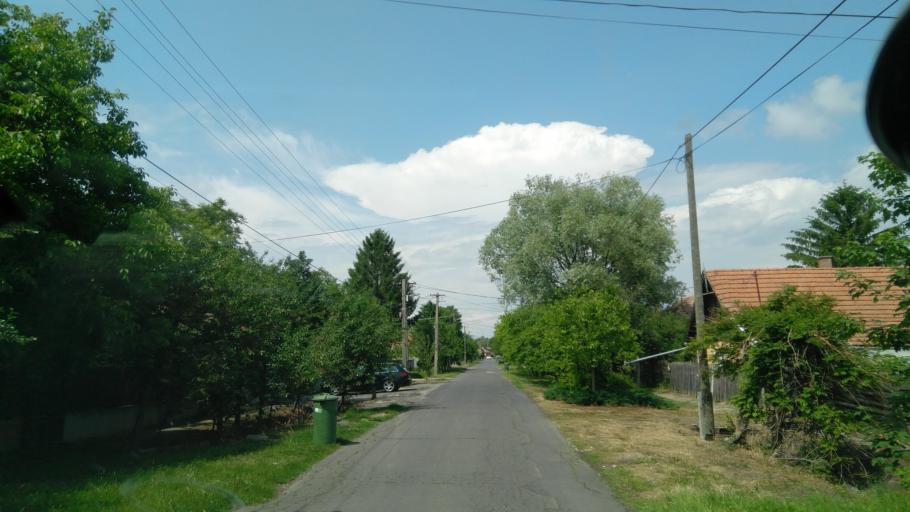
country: HU
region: Bekes
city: Bekes
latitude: 46.7607
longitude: 21.1473
